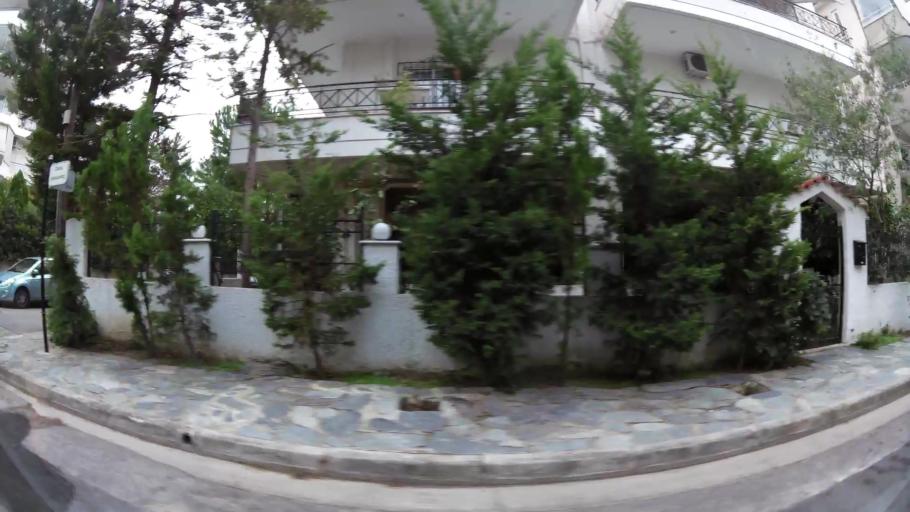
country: GR
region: Attica
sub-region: Nomarchia Athinas
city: Alimos
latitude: 37.9167
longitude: 23.7238
